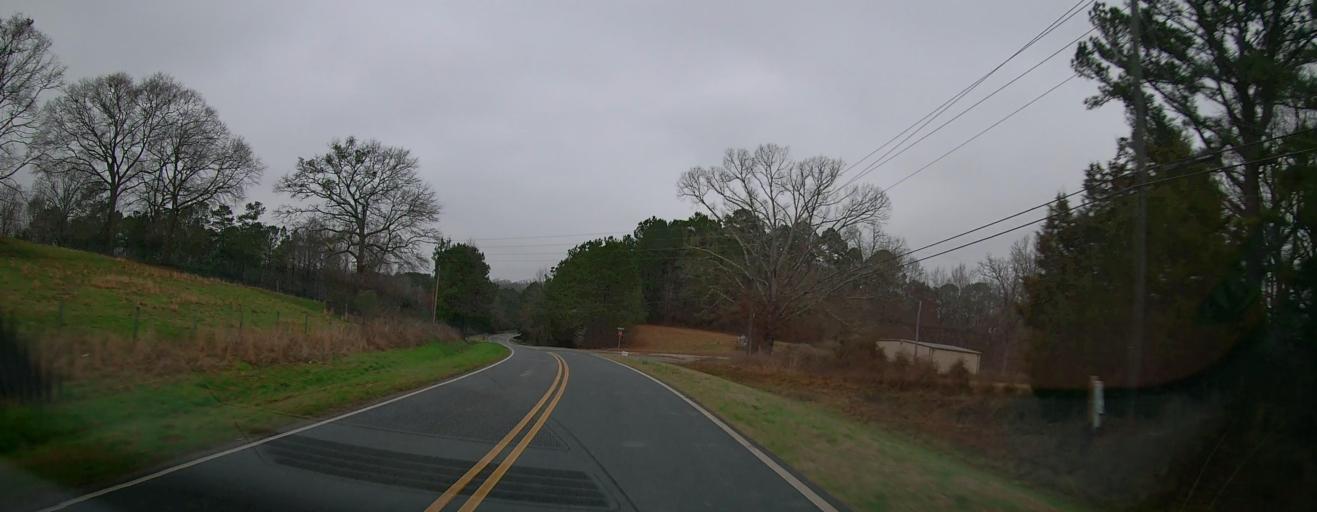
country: US
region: Georgia
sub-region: Pike County
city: Zebulon
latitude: 33.1227
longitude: -84.3448
